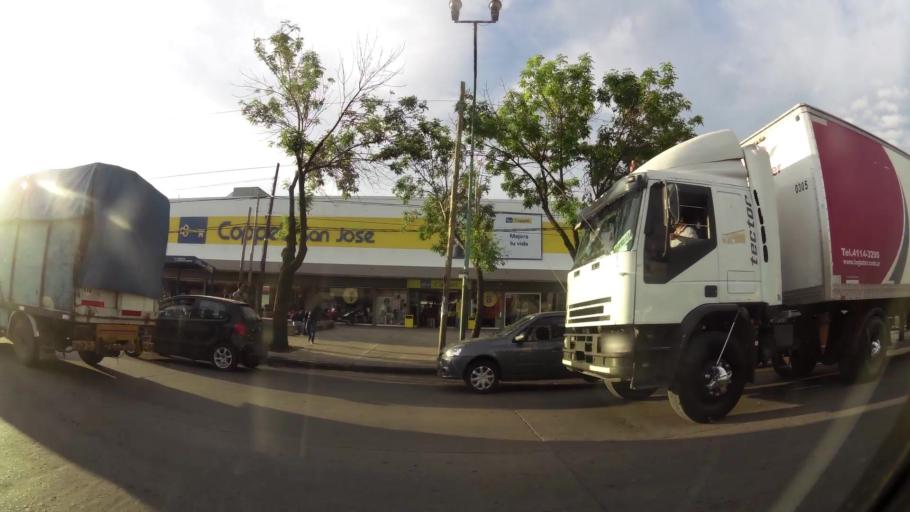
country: AR
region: Buenos Aires
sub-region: Partido de Lomas de Zamora
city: Lomas de Zamora
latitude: -34.7611
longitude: -58.3607
